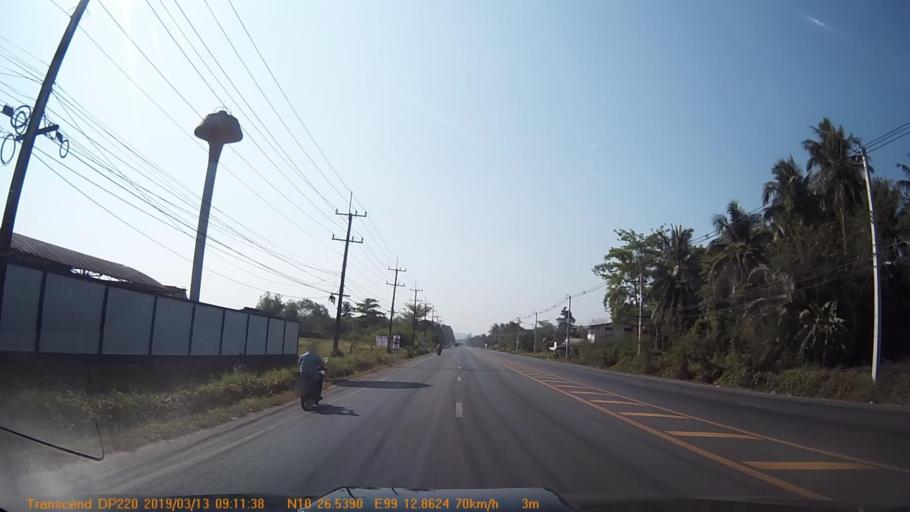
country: TH
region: Chumphon
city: Chumphon
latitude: 10.4421
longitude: 99.2145
